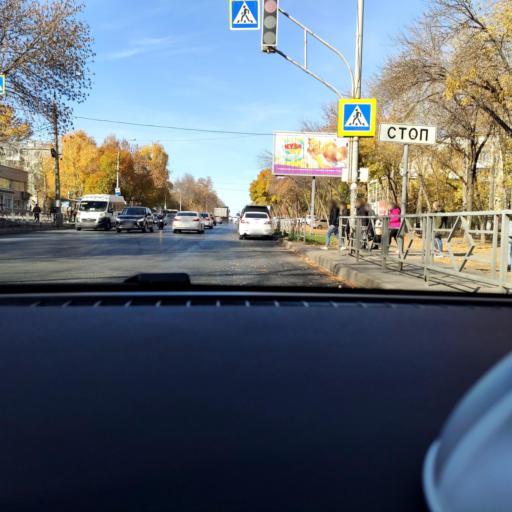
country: RU
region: Samara
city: Samara
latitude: 53.2160
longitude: 50.2100
